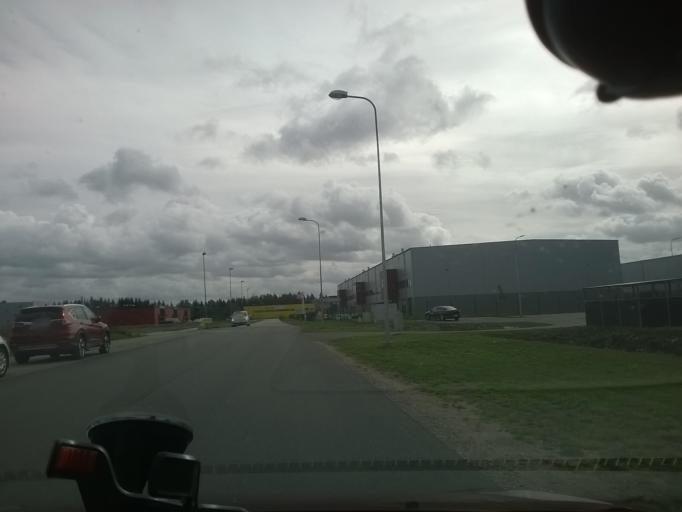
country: EE
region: Harju
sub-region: Rae vald
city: Jueri
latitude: 59.3875
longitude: 24.8246
